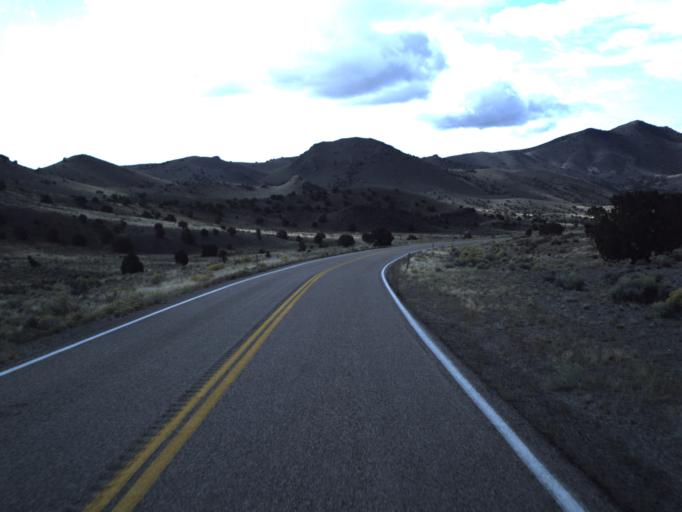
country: US
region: Utah
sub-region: Beaver County
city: Milford
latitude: 38.4516
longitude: -113.2595
